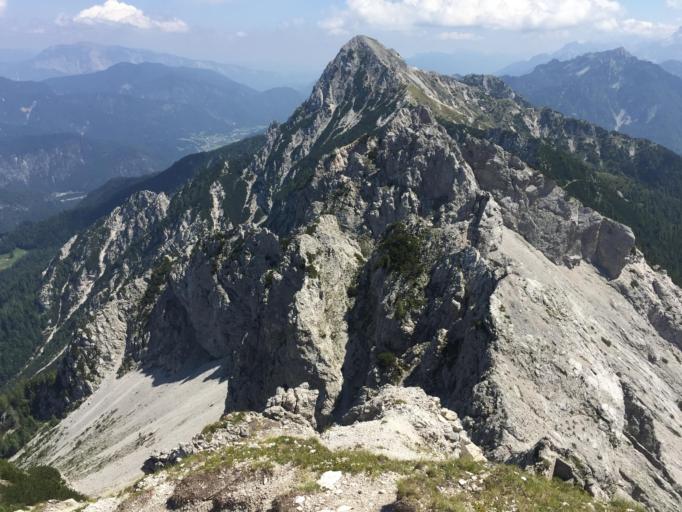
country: IT
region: Friuli Venezia Giulia
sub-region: Provincia di Udine
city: Malborghetto
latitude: 46.4734
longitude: 13.4355
